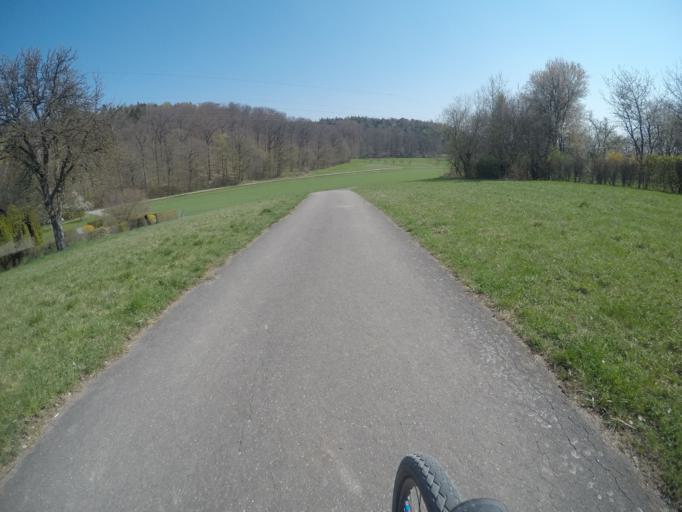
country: DE
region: Baden-Wuerttemberg
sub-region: Regierungsbezirk Stuttgart
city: Magstadt
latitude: 48.7525
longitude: 8.9686
